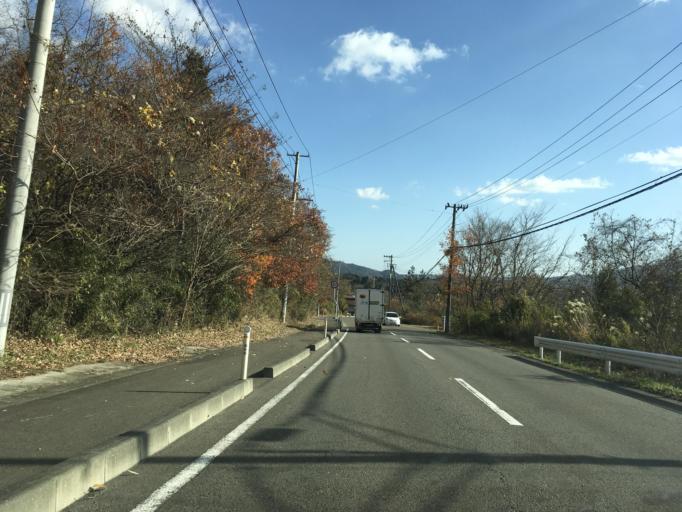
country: JP
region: Miyagi
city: Sendai
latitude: 38.2852
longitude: 140.7543
